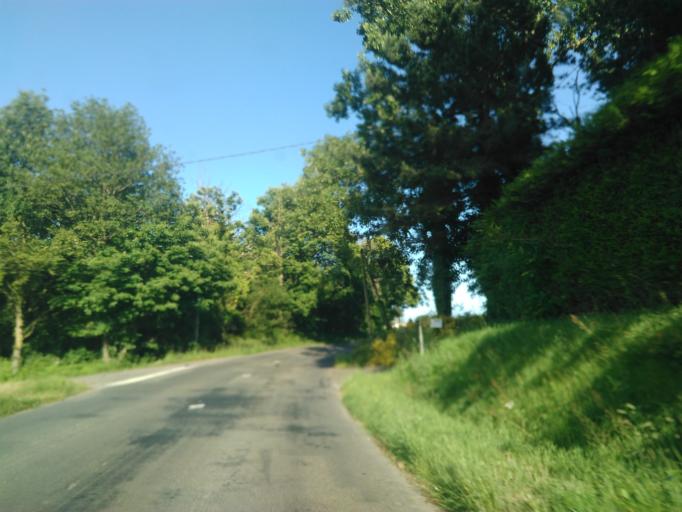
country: FR
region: Brittany
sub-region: Departement d'Ille-et-Vilaine
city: Geveze
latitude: 48.2249
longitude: -1.7739
